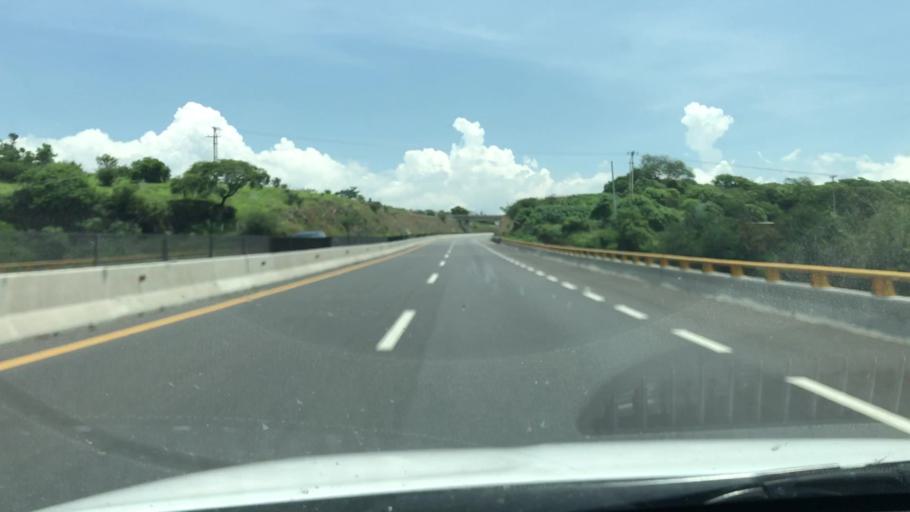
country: MX
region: Jalisco
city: Degollado
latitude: 20.3795
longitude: -102.1214
